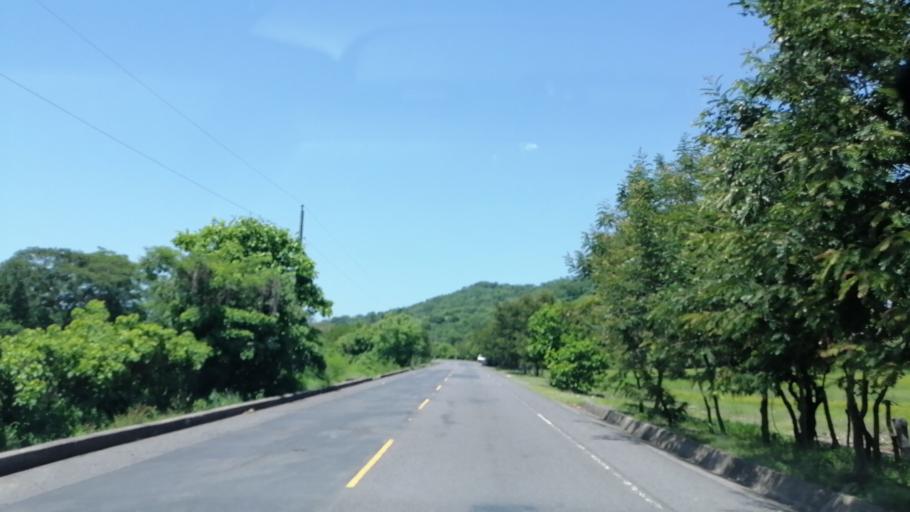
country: SV
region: Chalatenango
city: Chalatenango
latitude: 14.0324
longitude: -88.9594
